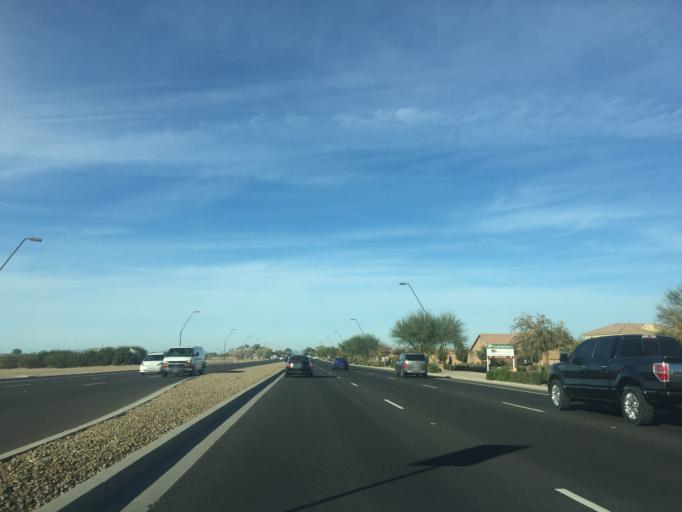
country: US
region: Arizona
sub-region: Maricopa County
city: Queen Creek
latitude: 33.2348
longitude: -111.6344
